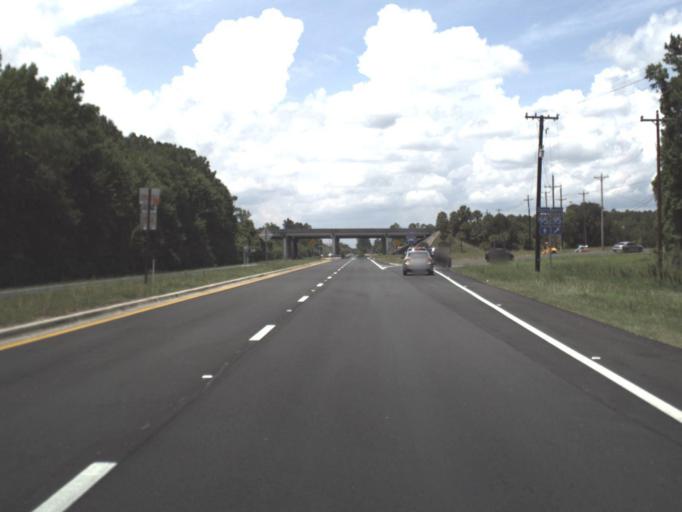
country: US
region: Georgia
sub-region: Camden County
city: Kingsland
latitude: 30.7089
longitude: -81.6696
